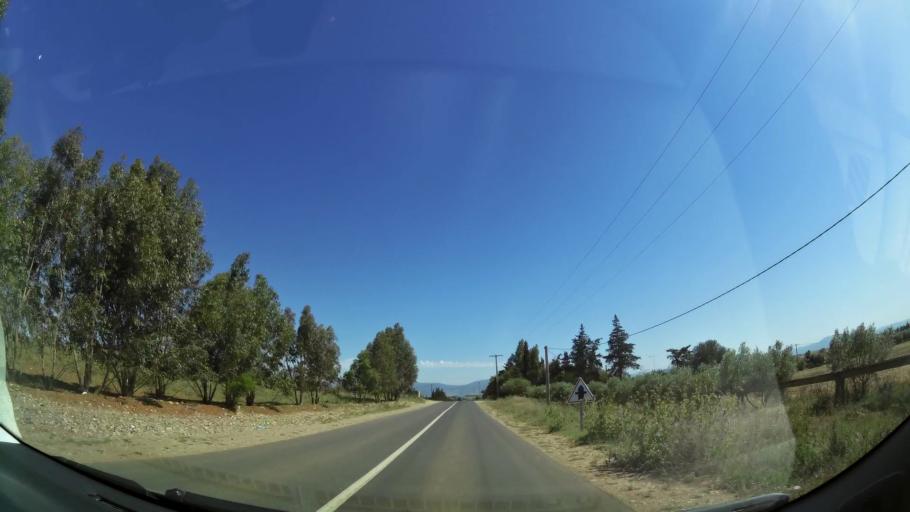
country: MA
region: Oriental
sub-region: Berkane-Taourirt
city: Madagh
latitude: 35.0274
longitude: -2.4117
